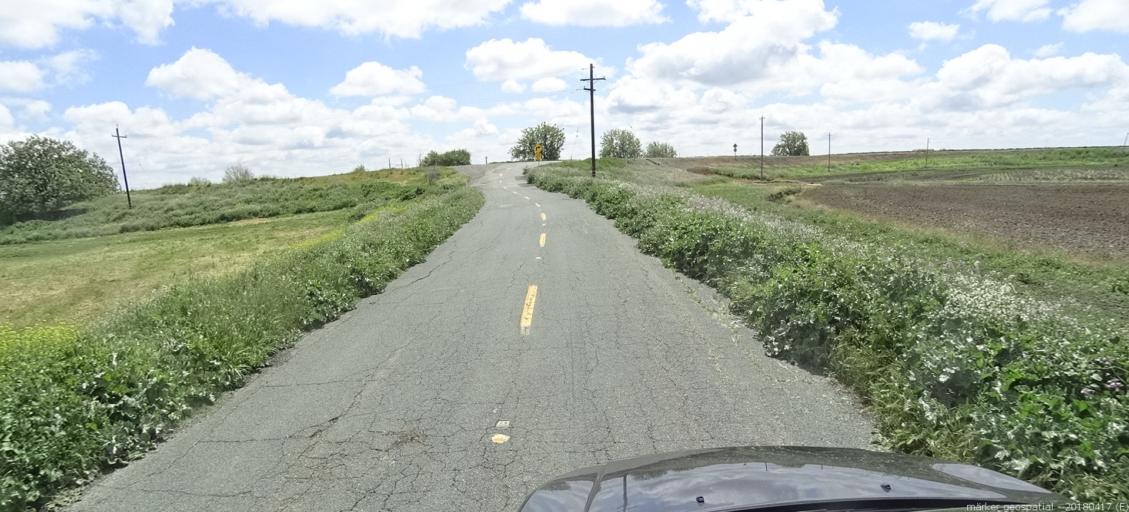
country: US
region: California
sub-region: Sacramento County
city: Walnut Grove
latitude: 38.1998
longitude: -121.5263
